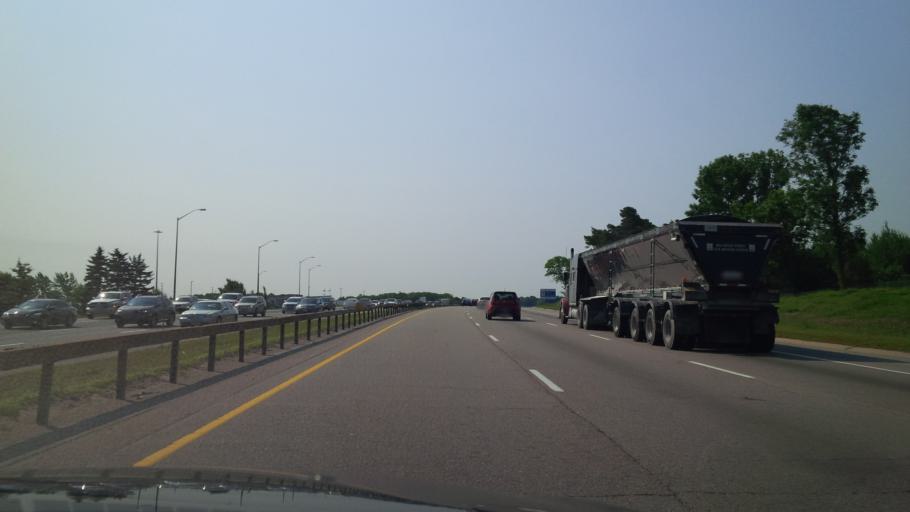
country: CA
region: Ontario
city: Barrie
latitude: 44.3551
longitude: -79.6904
